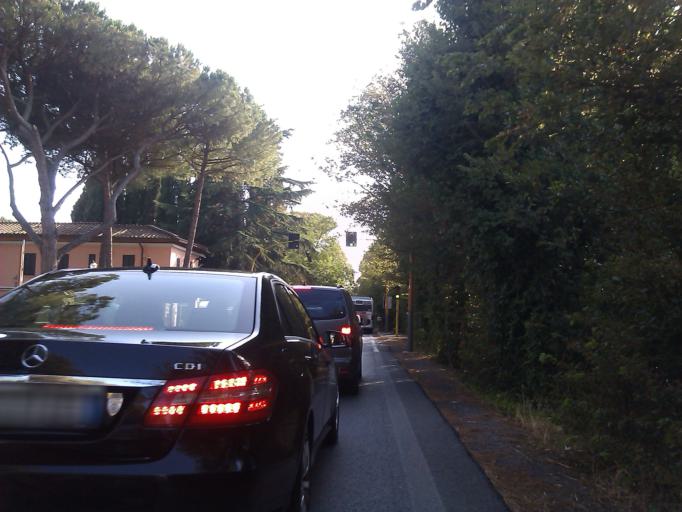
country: IT
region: Latium
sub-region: Citta metropolitana di Roma Capitale
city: Rome
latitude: 41.8329
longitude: 12.5360
